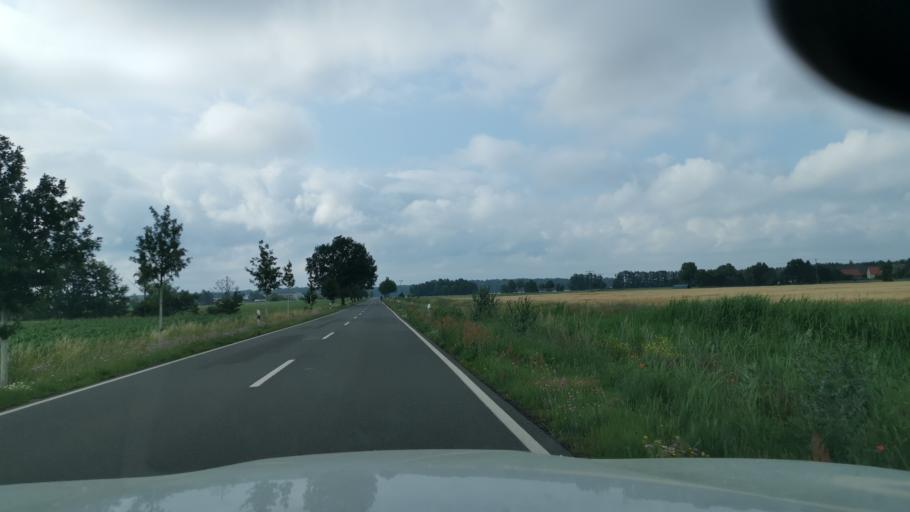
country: DE
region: Saxony-Anhalt
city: Annaburg
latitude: 51.7683
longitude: 13.0290
